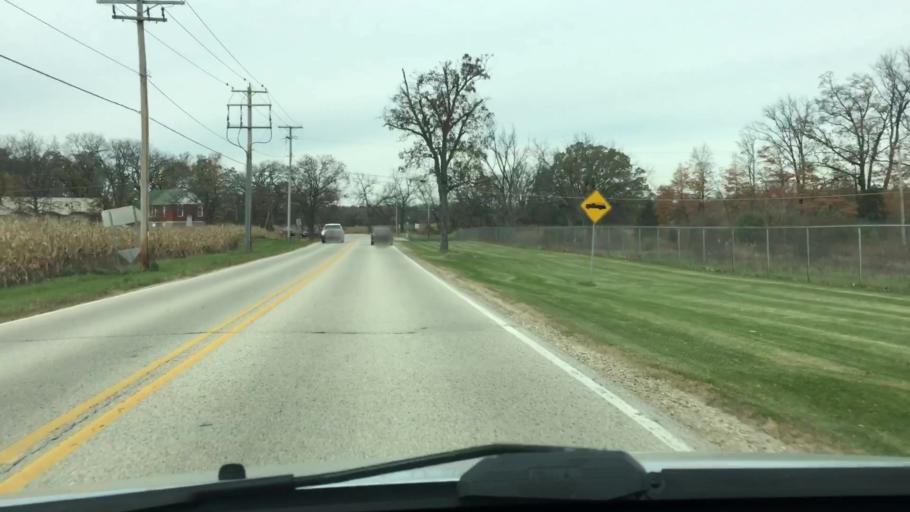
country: US
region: Wisconsin
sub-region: Waukesha County
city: North Prairie
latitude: 42.8924
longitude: -88.3837
